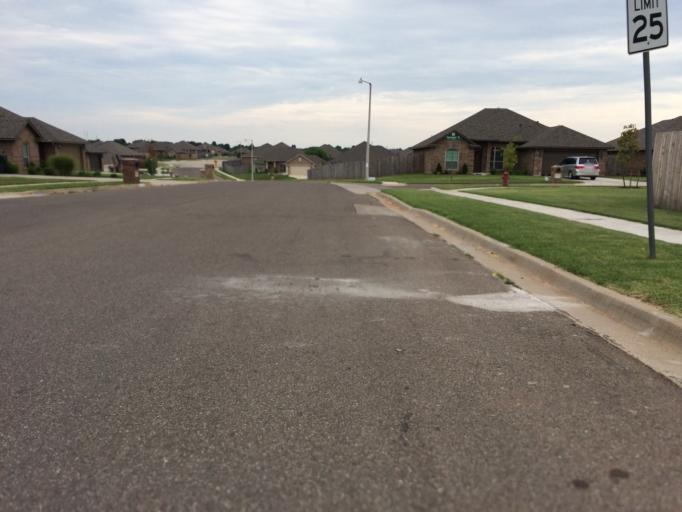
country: US
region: Oklahoma
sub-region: Cleveland County
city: Hall Park
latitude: 35.2472
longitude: -97.4190
